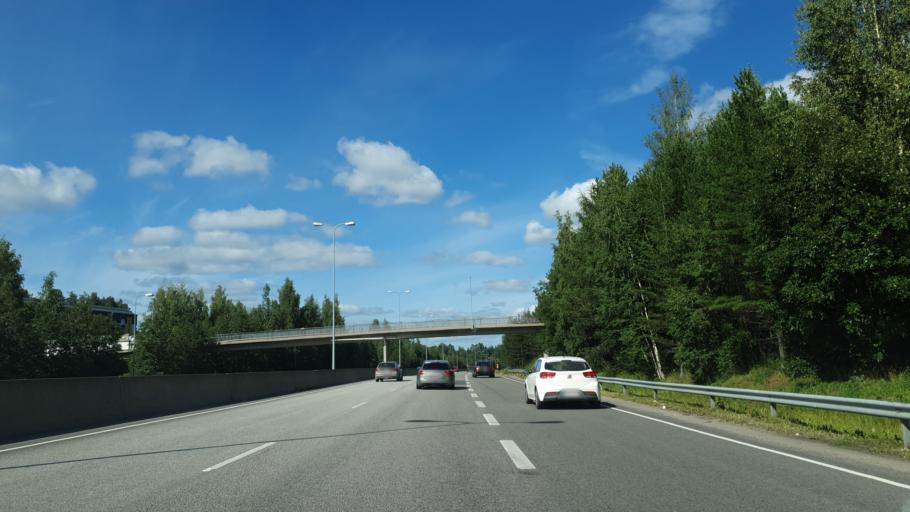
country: FI
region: Central Finland
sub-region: Jyvaeskylae
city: Jyvaeskylae
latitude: 62.2196
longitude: 25.7250
